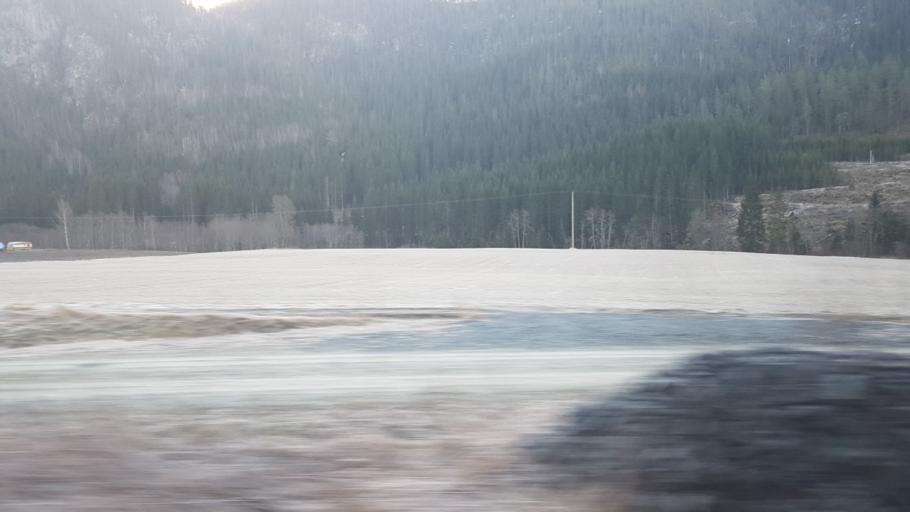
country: NO
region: Nord-Trondelag
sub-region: Stjordal
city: Stjordalshalsen
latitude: 63.5914
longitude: 11.0141
